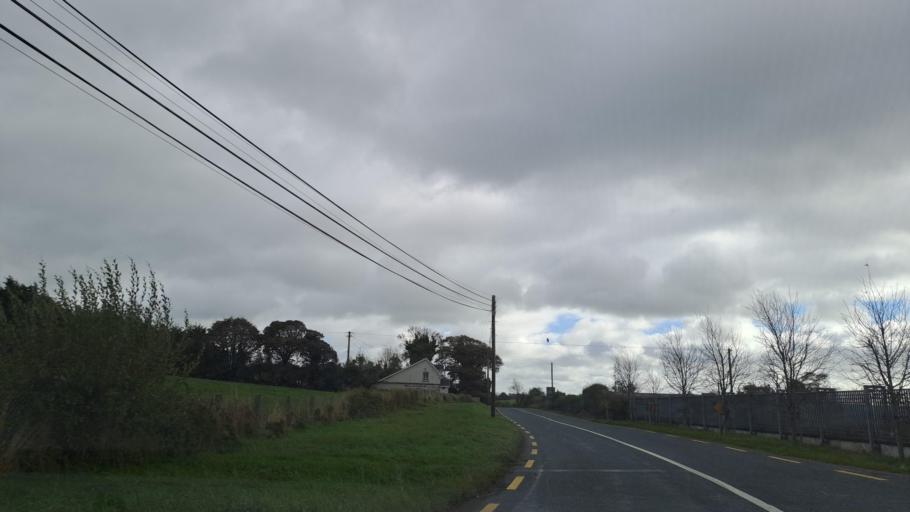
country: IE
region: Ulster
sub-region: An Cabhan
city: Kingscourt
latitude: 53.9115
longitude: -6.8458
